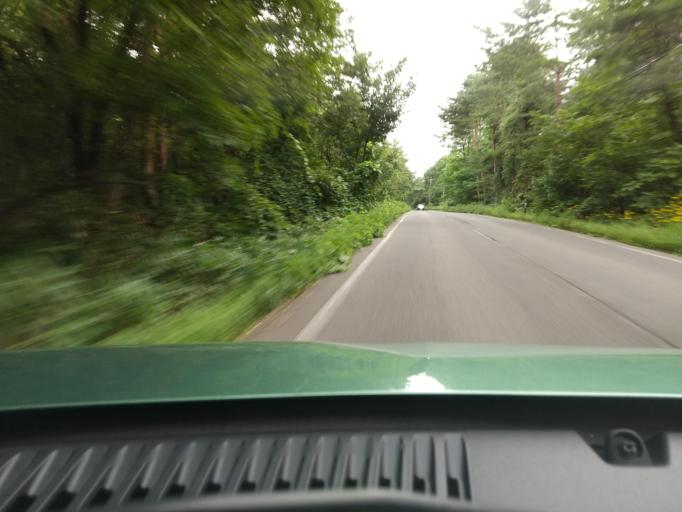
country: JP
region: Akita
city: Akita
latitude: 39.7667
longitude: 140.1338
